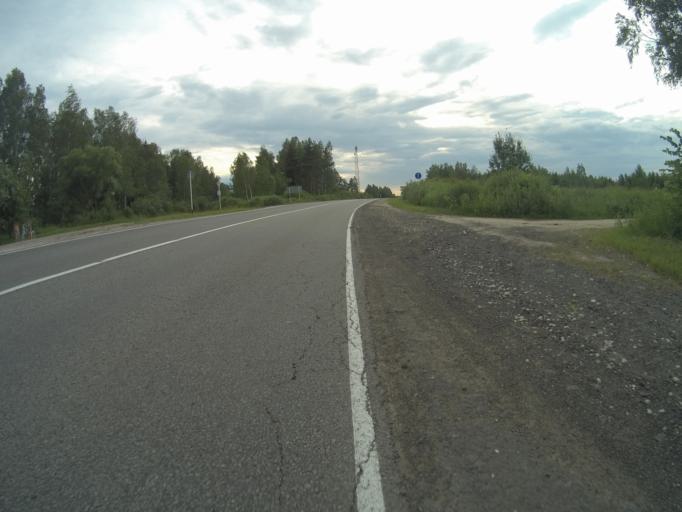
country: RU
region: Vladimir
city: Sudogda
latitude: 55.9763
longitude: 40.7451
